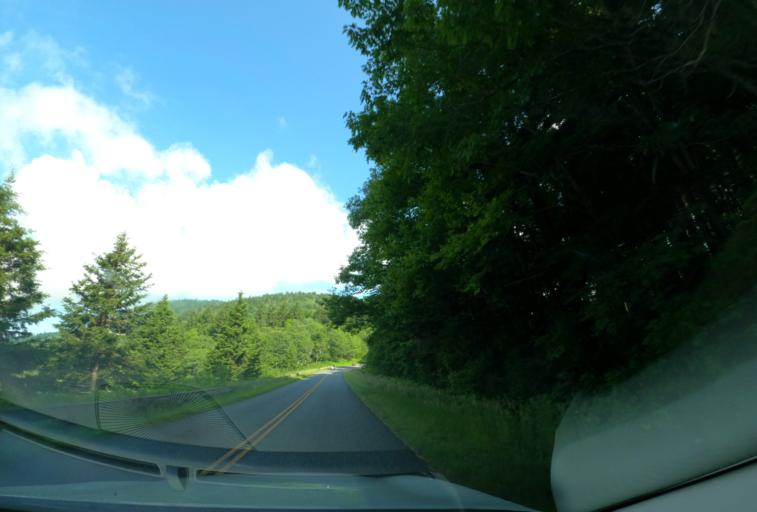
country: US
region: North Carolina
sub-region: Haywood County
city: Hazelwood
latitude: 35.3128
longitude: -82.9533
